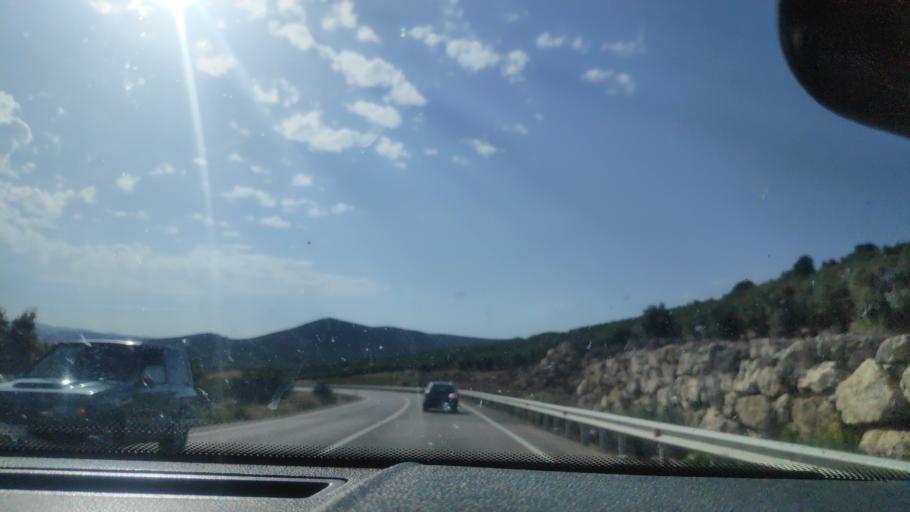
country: ES
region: Andalusia
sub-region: Provincia de Jaen
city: Frailes
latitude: 37.4426
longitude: -3.8291
